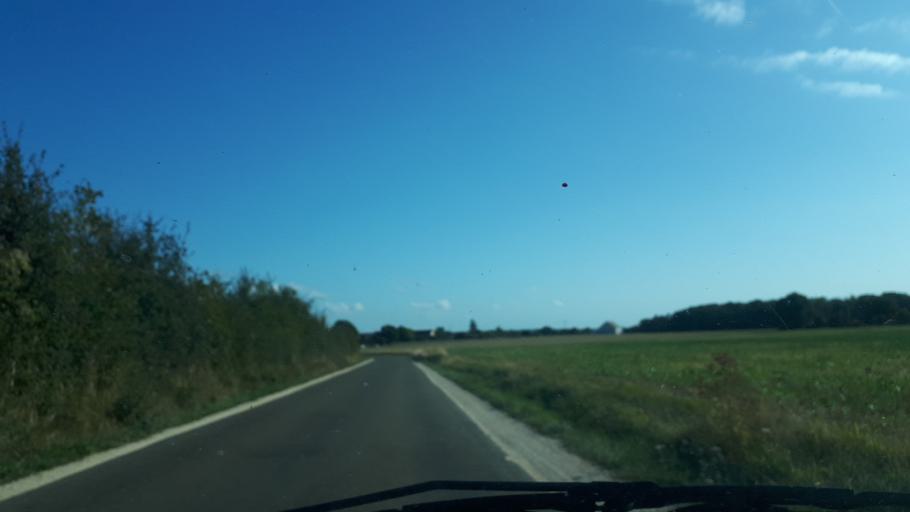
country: FR
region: Centre
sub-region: Departement du Loir-et-Cher
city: Mondoubleau
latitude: 47.9909
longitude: 0.9233
